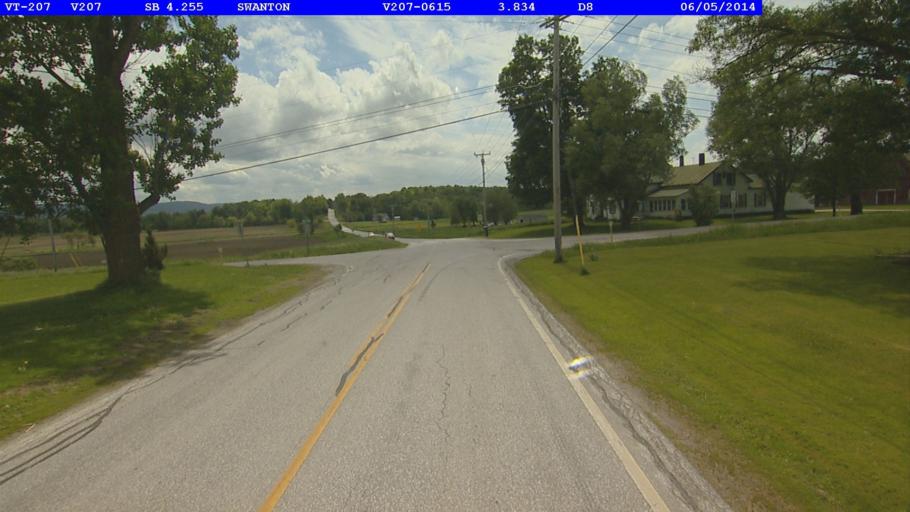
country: US
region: Vermont
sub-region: Franklin County
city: Swanton
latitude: 44.8993
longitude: -73.0666
